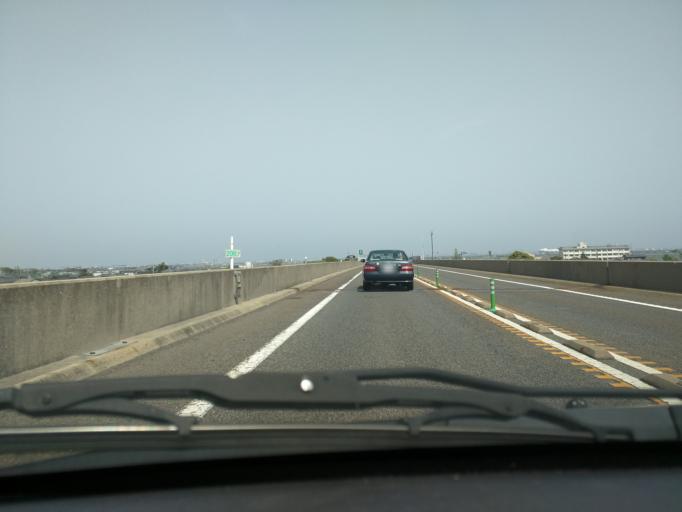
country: JP
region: Niigata
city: Kameda-honcho
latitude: 37.8331
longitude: 139.0718
